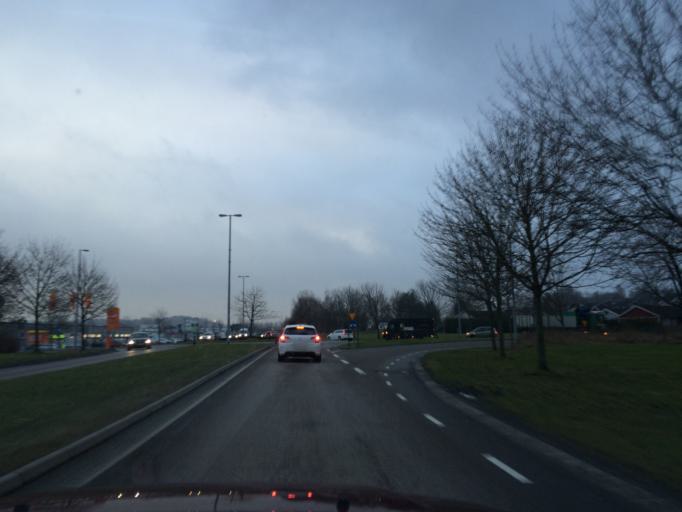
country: SE
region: Halland
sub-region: Kungsbacka Kommun
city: Kungsbacka
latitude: 57.5059
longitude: 12.0664
